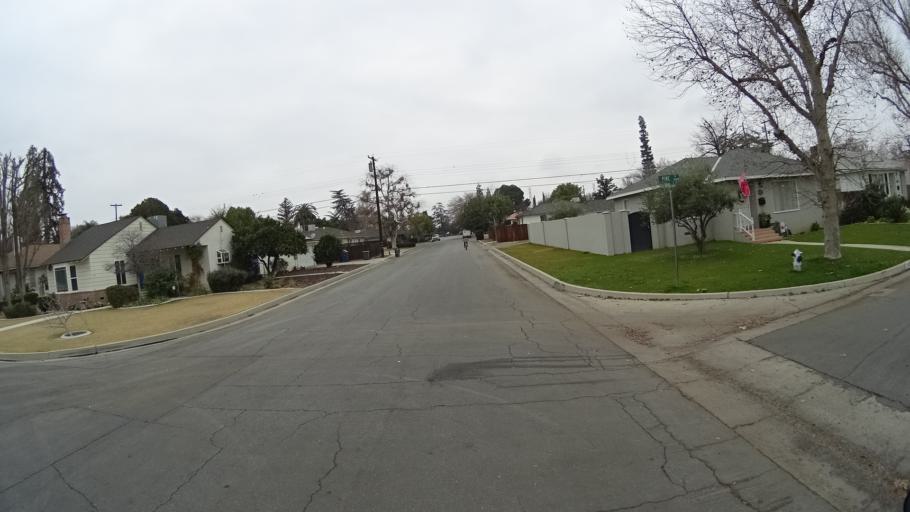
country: US
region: California
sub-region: Kern County
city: Bakersfield
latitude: 35.3855
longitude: -119.0293
